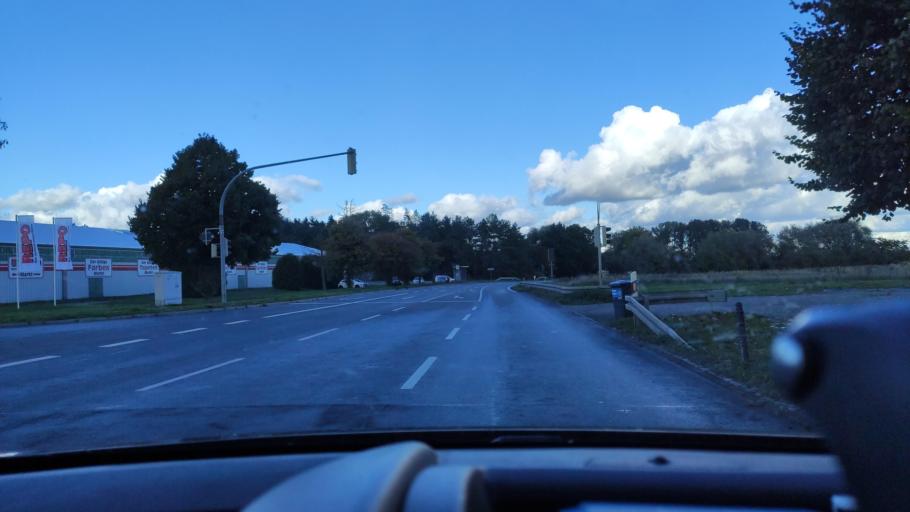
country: DE
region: Mecklenburg-Vorpommern
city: Tarnow
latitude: 53.7642
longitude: 12.0524
